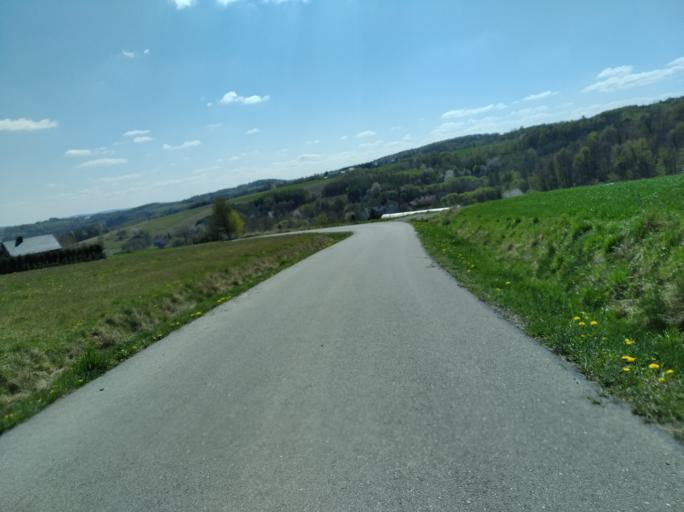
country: PL
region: Subcarpathian Voivodeship
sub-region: Powiat strzyzowski
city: Wisniowa
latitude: 49.9098
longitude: 21.6639
